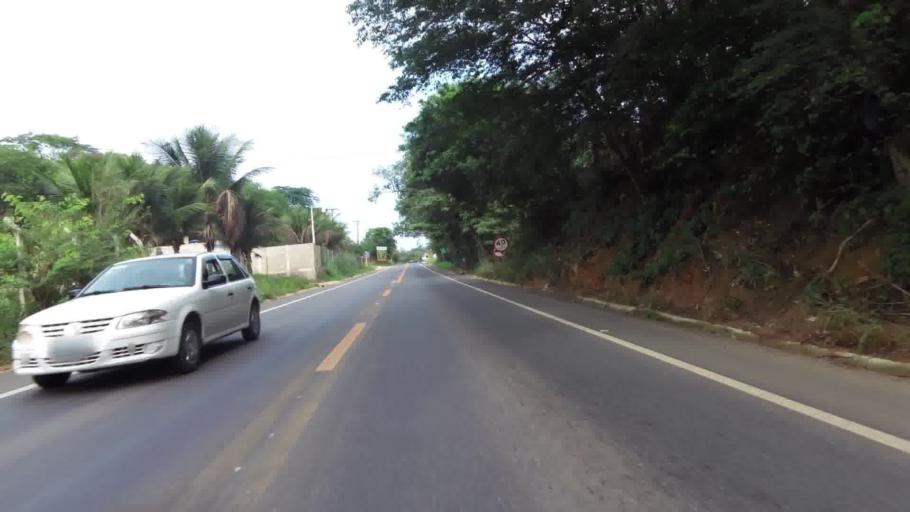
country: BR
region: Espirito Santo
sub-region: Piuma
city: Piuma
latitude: -20.8146
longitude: -40.6872
